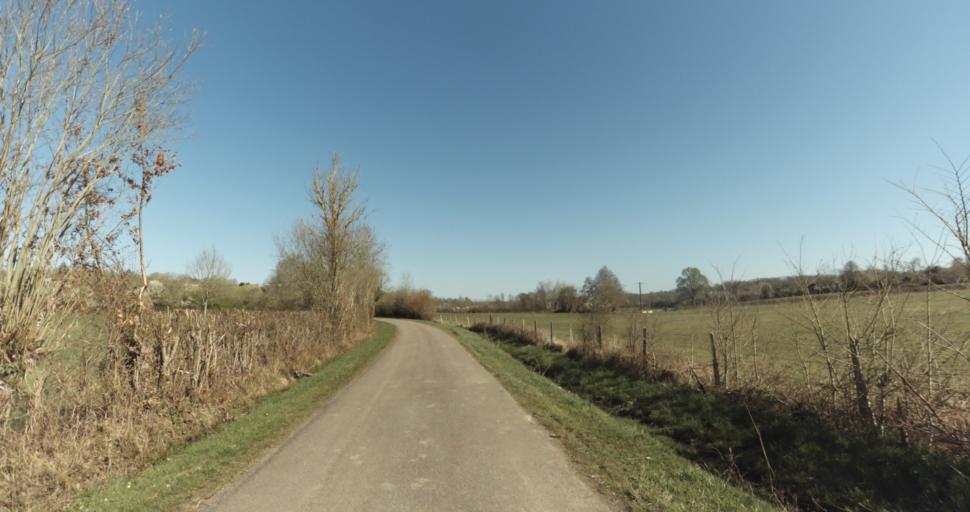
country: FR
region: Lower Normandy
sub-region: Departement du Calvados
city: Livarot
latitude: 48.9854
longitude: 0.0613
